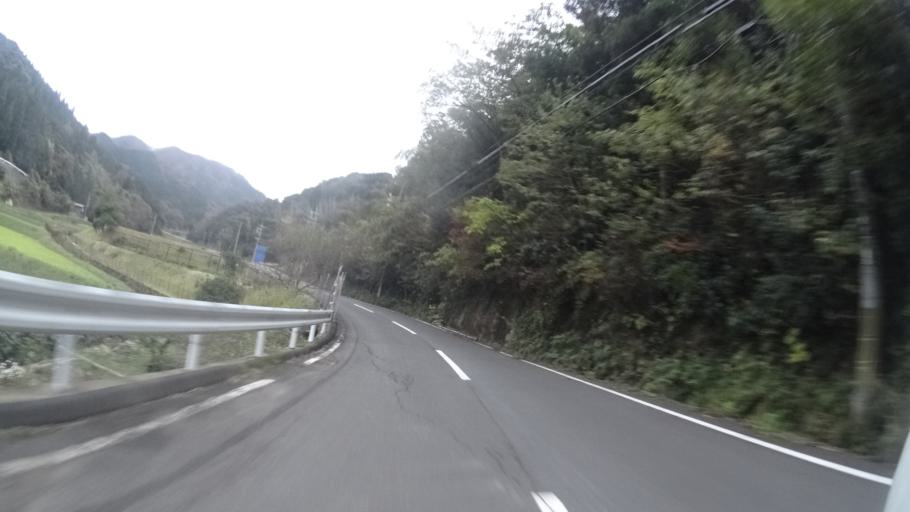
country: JP
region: Kyoto
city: Maizuru
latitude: 35.5640
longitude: 135.4539
